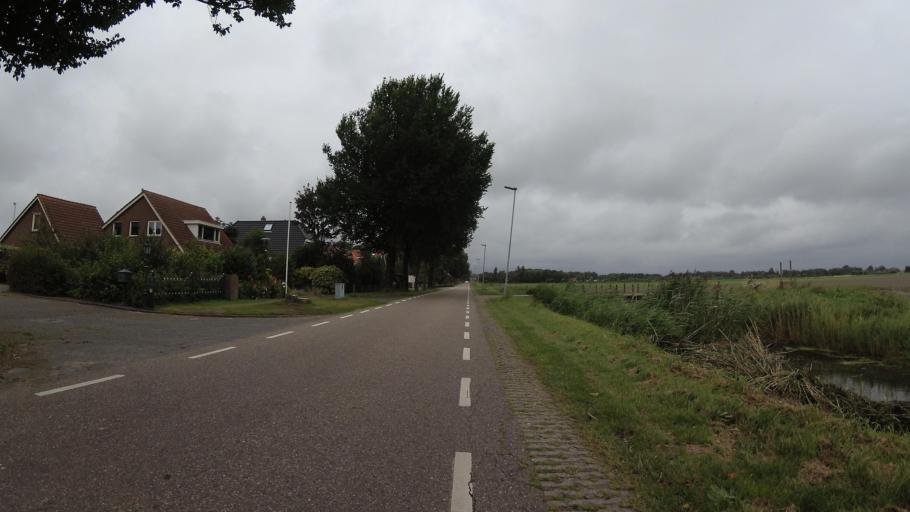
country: NL
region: North Holland
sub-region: Gemeente Den Helder
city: Den Helder
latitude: 52.9243
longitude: 4.7720
